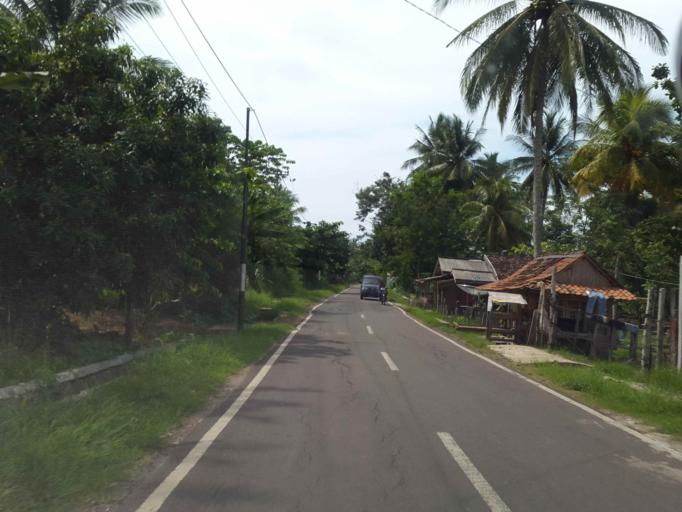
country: ID
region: Banten
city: Citeureup
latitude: -6.5284
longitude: 105.7059
